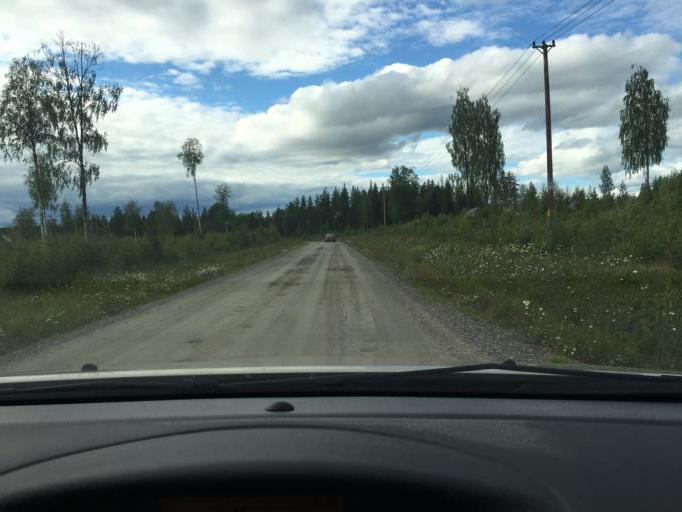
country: SE
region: Norrbotten
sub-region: Overkalix Kommun
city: OEverkalix
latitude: 66.0907
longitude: 22.8324
